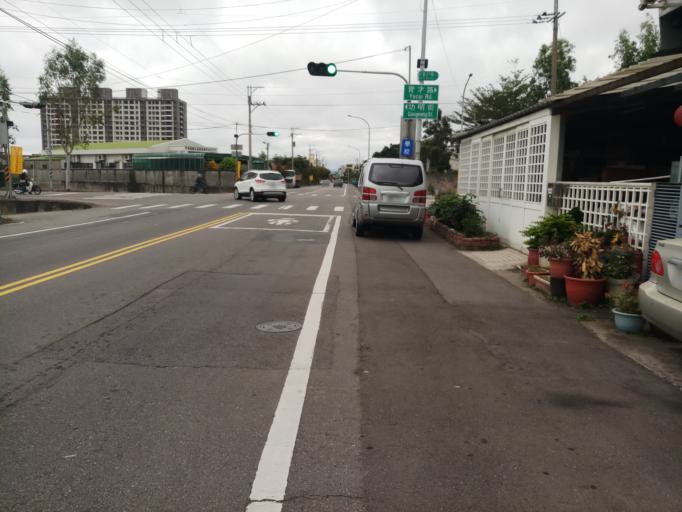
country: TW
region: Taiwan
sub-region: Miaoli
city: Miaoli
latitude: 24.6789
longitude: 120.8623
